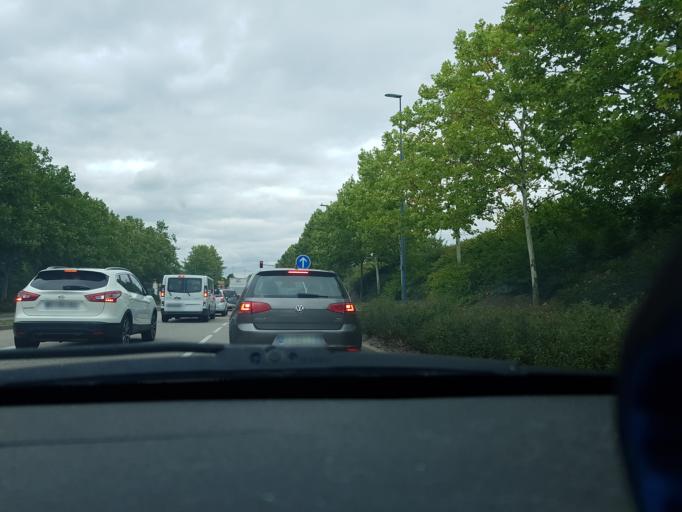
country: FR
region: Lorraine
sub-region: Departement de Meurthe-et-Moselle
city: Tomblaine
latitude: 48.6810
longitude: 6.2145
